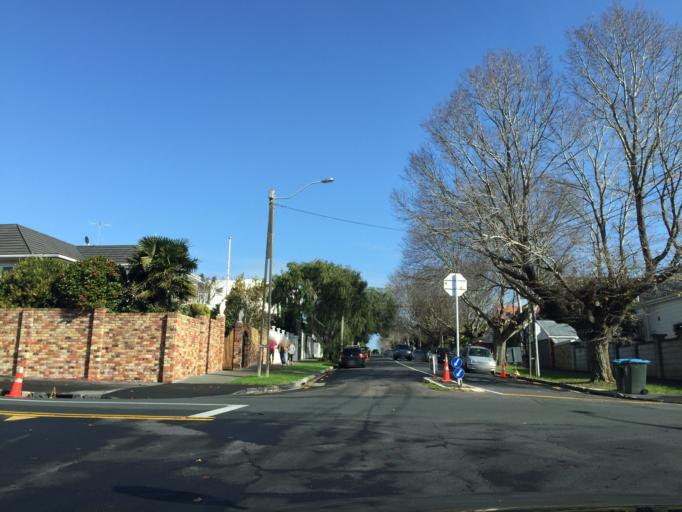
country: NZ
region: Auckland
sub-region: Auckland
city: Auckland
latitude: -36.8409
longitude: 174.7397
